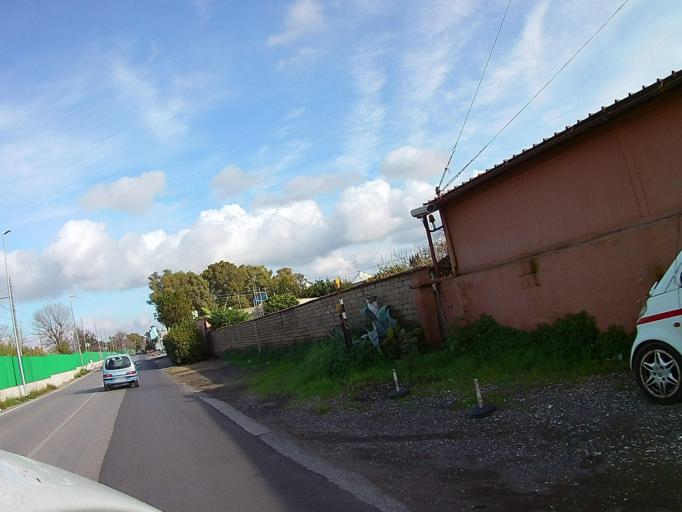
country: IT
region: Latium
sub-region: Citta metropolitana di Roma Capitale
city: Acilia-Castel Fusano-Ostia Antica
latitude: 41.7659
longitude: 12.3190
